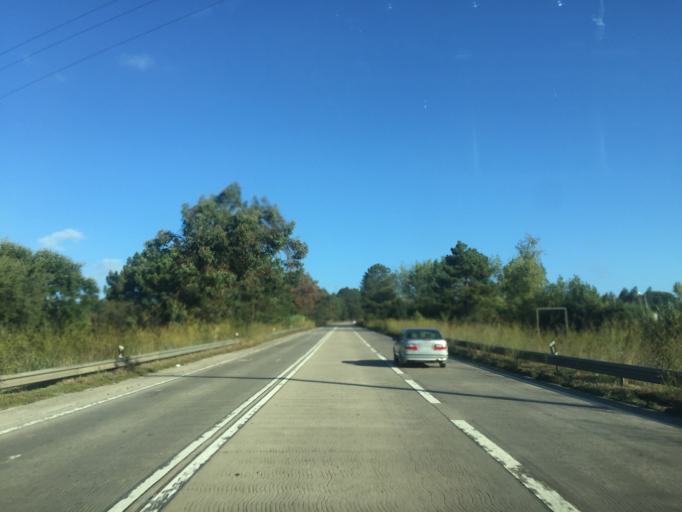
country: PT
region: Santarem
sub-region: Rio Maior
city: Rio Maior
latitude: 39.2970
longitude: -8.9480
